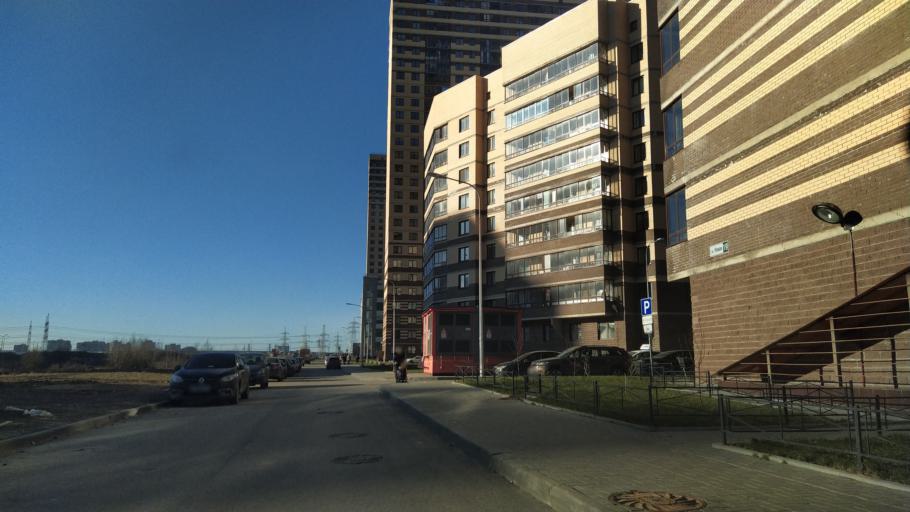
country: RU
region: Leningrad
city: Murino
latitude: 60.0380
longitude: 30.4568
